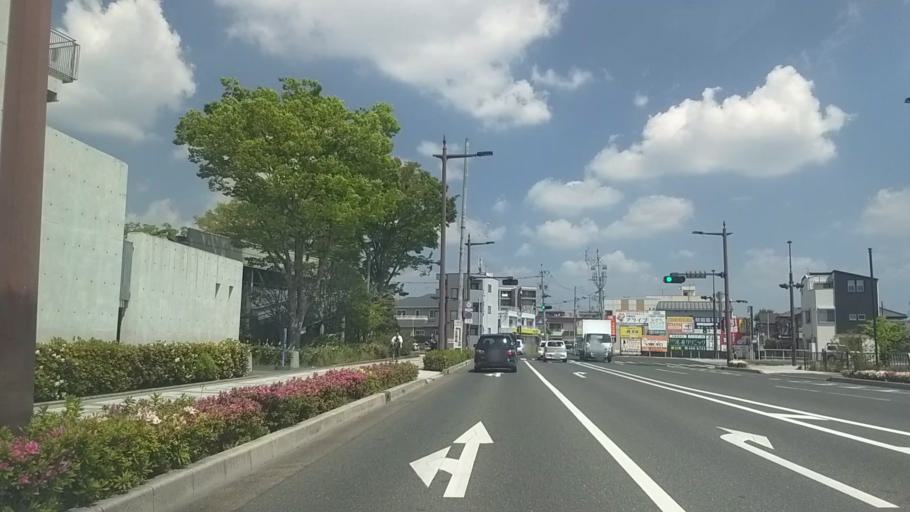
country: JP
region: Shizuoka
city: Hamamatsu
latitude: 34.7125
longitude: 137.7407
